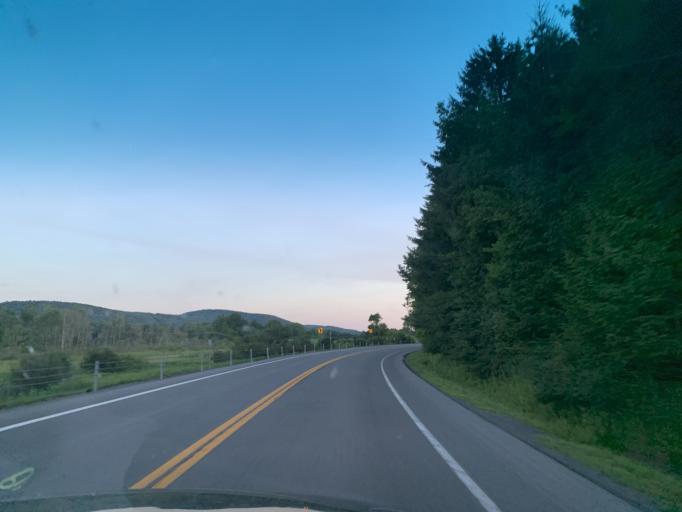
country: US
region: New York
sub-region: Oneida County
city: Waterville
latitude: 42.7936
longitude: -75.2565
